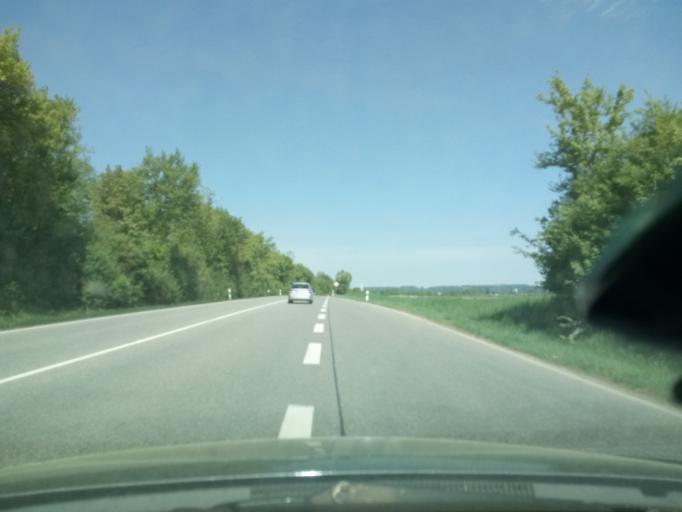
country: DE
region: Bavaria
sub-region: Upper Bavaria
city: Altoetting
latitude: 48.2213
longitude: 12.6938
